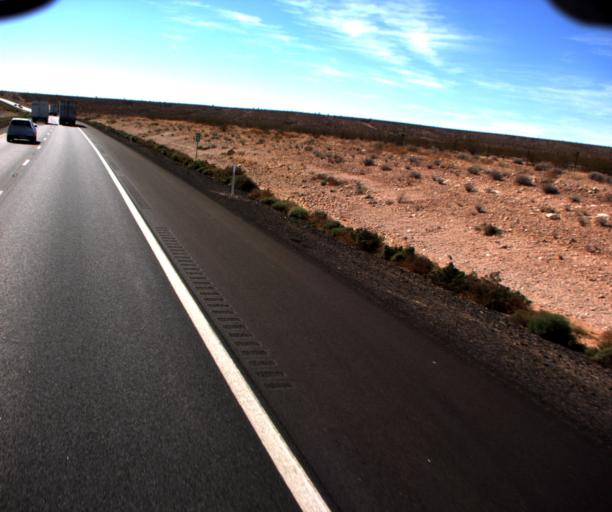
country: US
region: Arizona
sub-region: Mohave County
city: Beaver Dam
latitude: 36.8595
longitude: -113.9805
